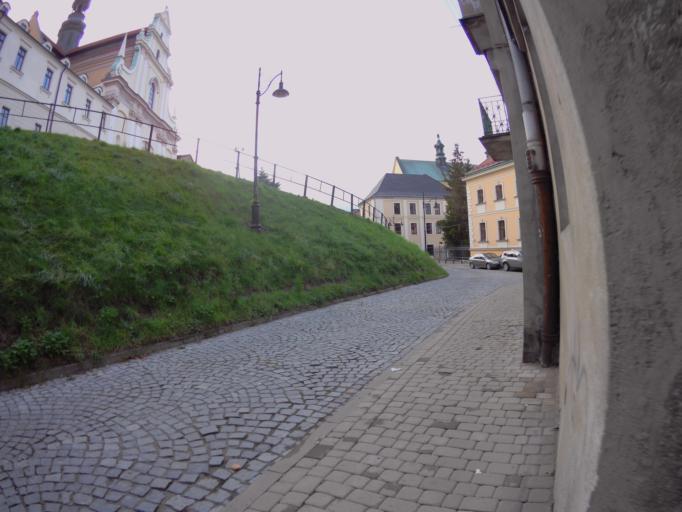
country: PL
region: Subcarpathian Voivodeship
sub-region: Przemysl
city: Przemysl
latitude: 49.7805
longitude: 22.7720
